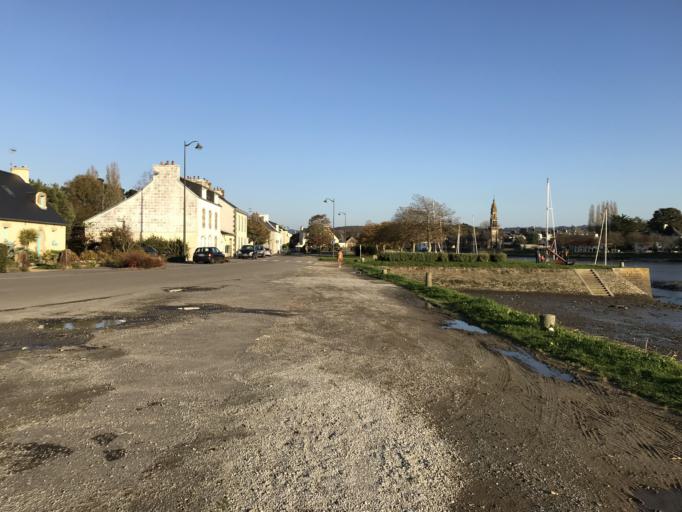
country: FR
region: Brittany
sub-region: Departement du Finistere
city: Le Faou
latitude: 48.2967
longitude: -4.1863
